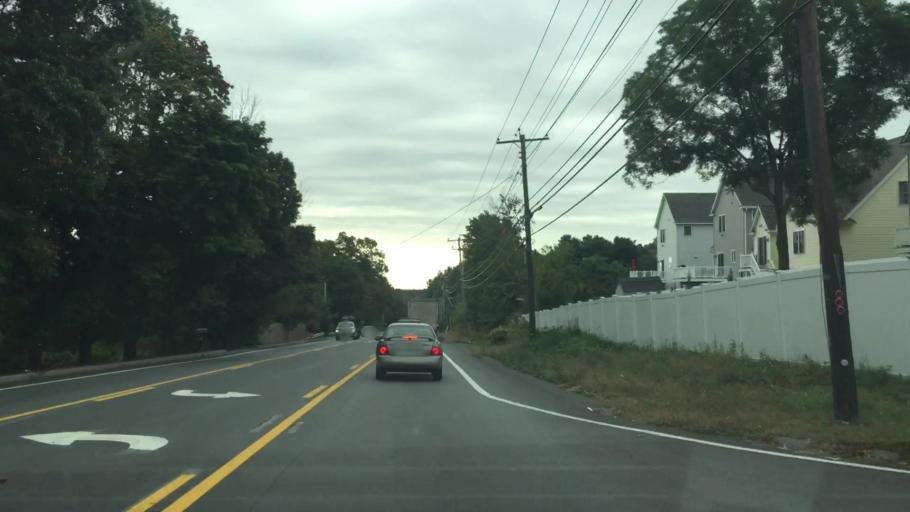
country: US
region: Massachusetts
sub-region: Essex County
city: Andover
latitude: 42.6555
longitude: -71.1015
